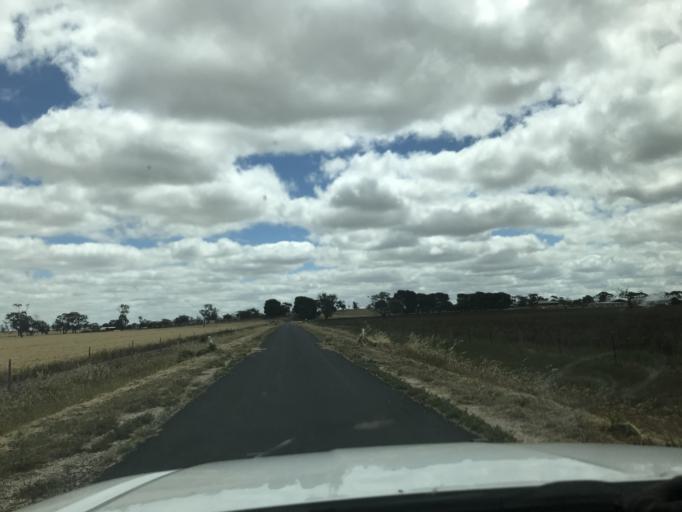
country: AU
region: South Australia
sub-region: Tatiara
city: Bordertown
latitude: -36.3565
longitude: 141.1889
